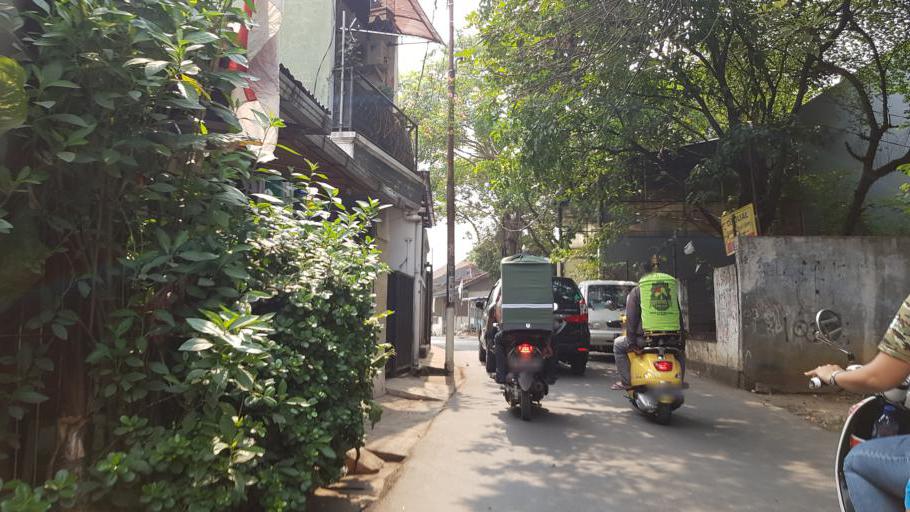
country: ID
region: West Java
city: Pamulang
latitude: -6.3294
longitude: 106.7894
